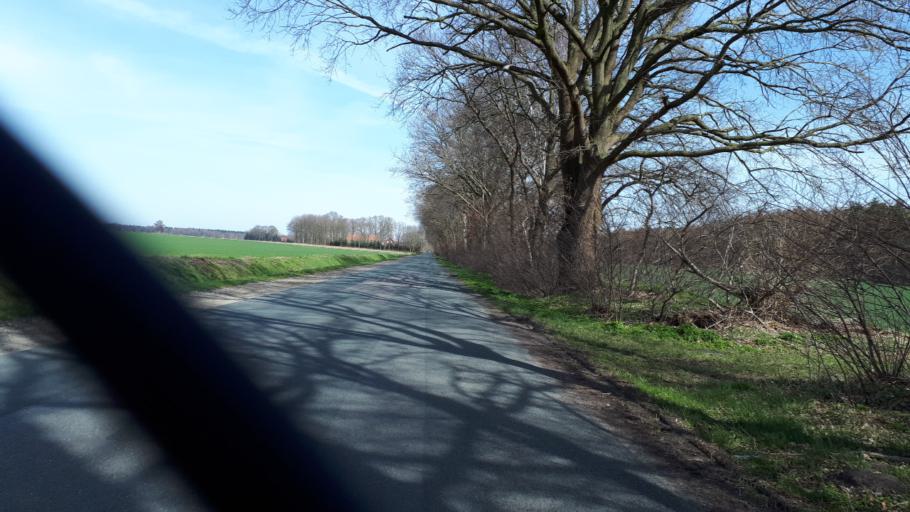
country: DE
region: Lower Saxony
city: Cloppenburg
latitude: 52.8710
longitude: 7.9978
